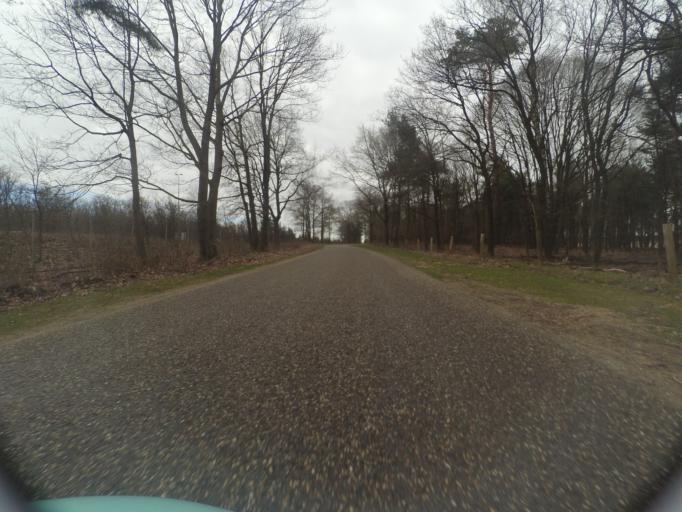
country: NL
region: Gelderland
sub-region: Gemeente Apeldoorn
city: Beekbergen
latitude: 52.0893
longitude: 5.9497
